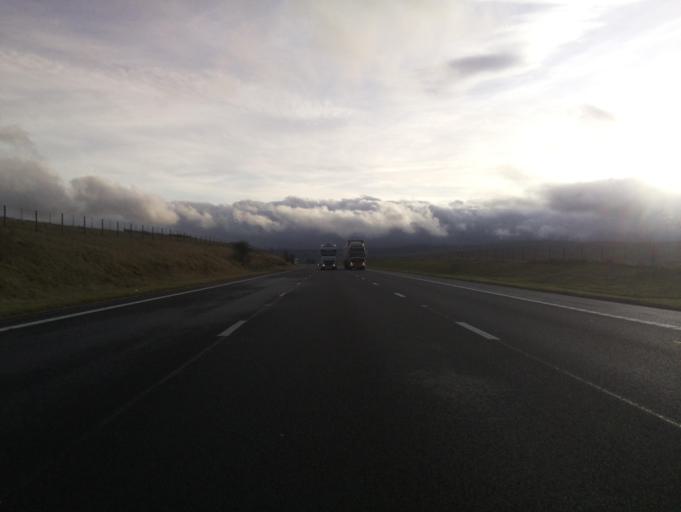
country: GB
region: England
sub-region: Cumbria
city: Appleby-in-Westmorland
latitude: 54.4797
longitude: -2.6355
